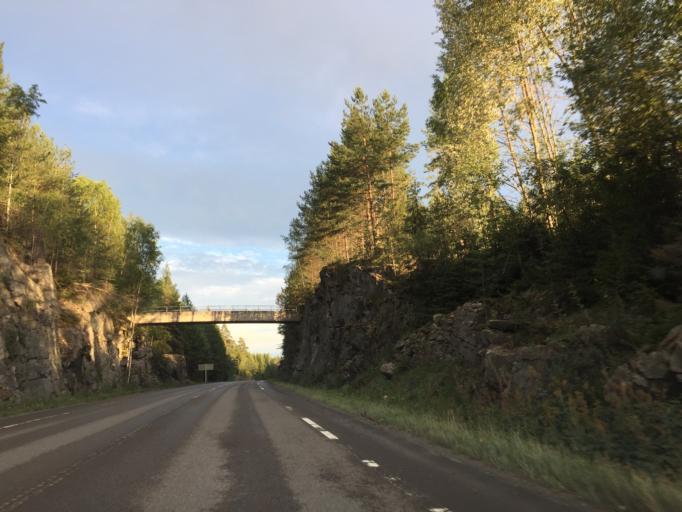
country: NO
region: Akershus
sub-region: Oppegard
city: Kolbotn
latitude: 59.7809
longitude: 10.8447
